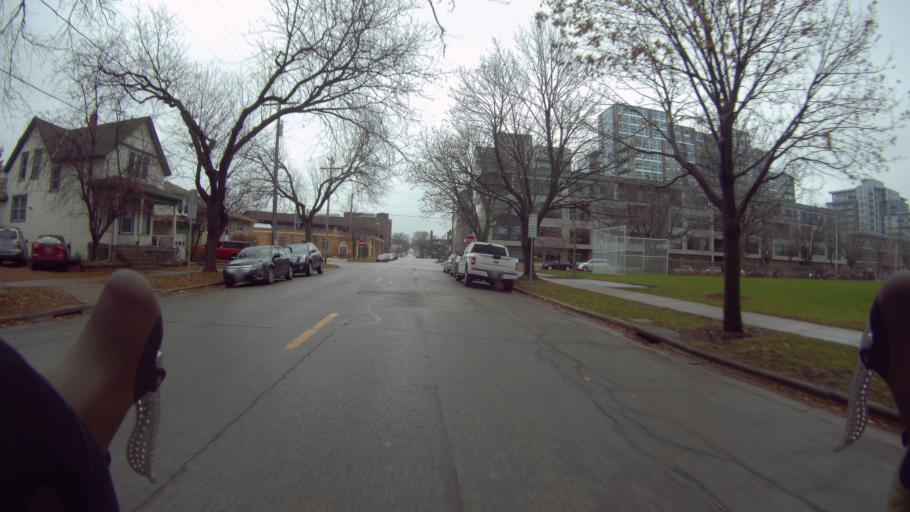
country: US
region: Wisconsin
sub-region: Dane County
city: Madison
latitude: 43.0836
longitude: -89.3750
